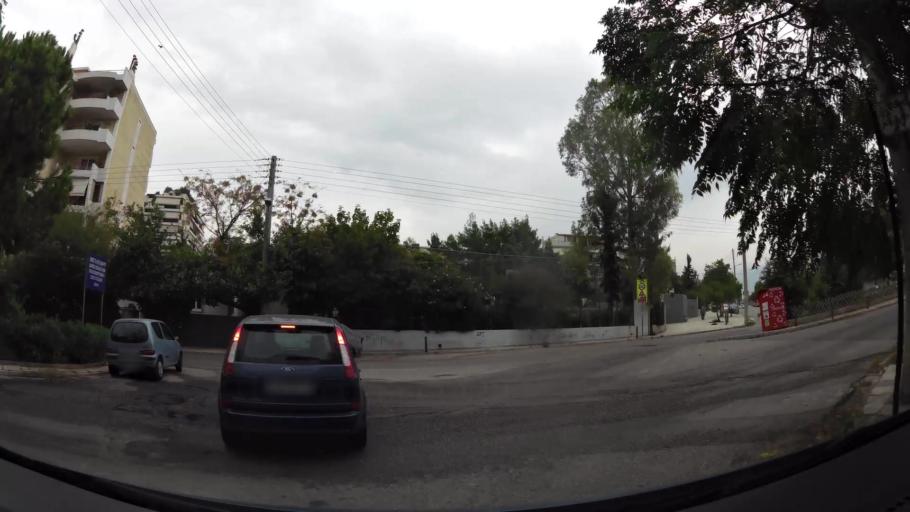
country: GR
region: Attica
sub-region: Nomarchia Athinas
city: Palaio Faliro
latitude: 37.9193
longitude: 23.7109
